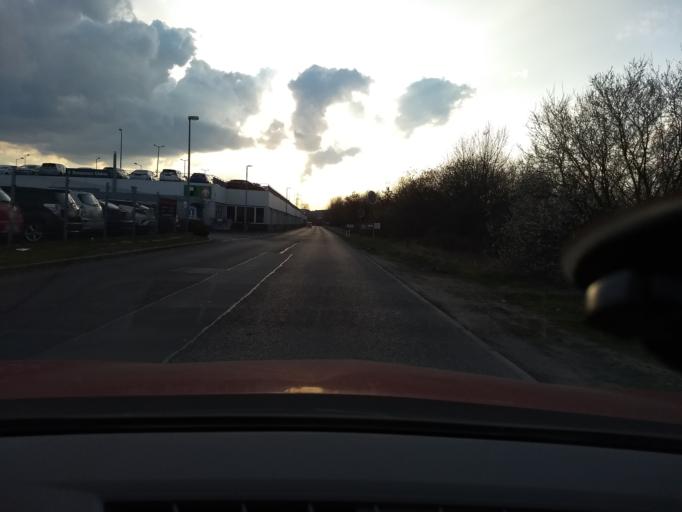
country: CZ
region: Central Bohemia
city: Hostivice
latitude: 50.0535
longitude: 14.3014
